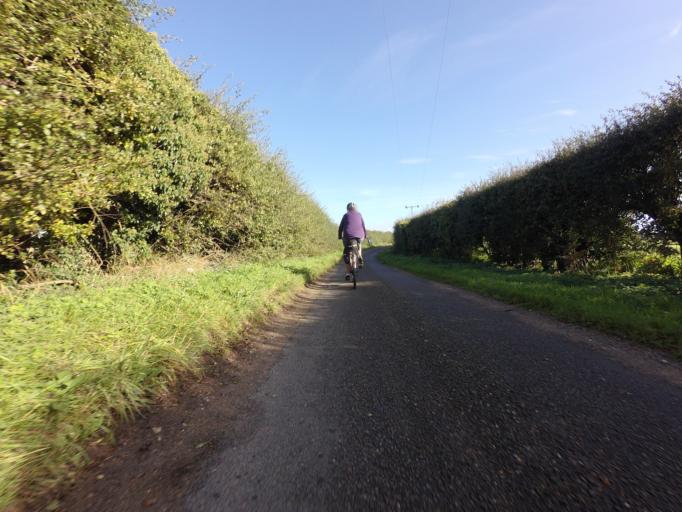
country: GB
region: England
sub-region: Norfolk
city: Fakenham
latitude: 52.8391
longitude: 0.6787
